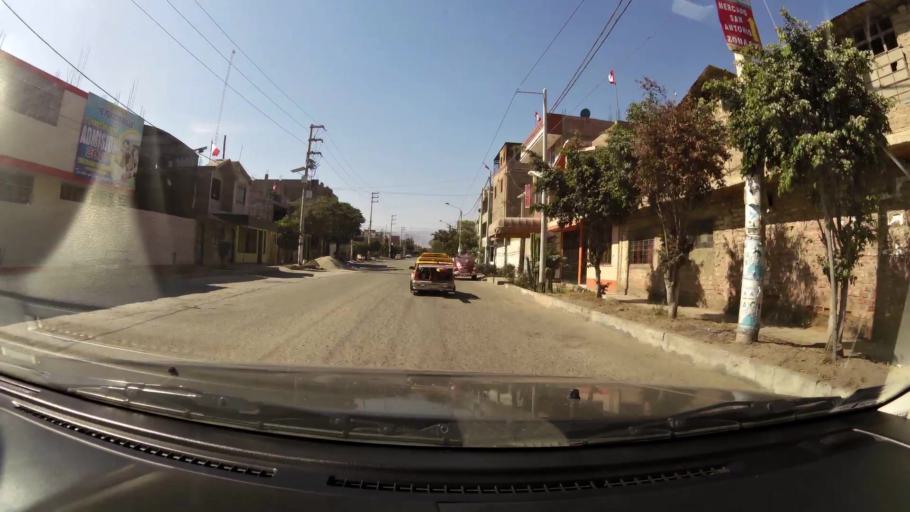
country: PE
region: Ica
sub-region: Provincia de Ica
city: La Tinguina
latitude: -14.0496
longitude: -75.7022
